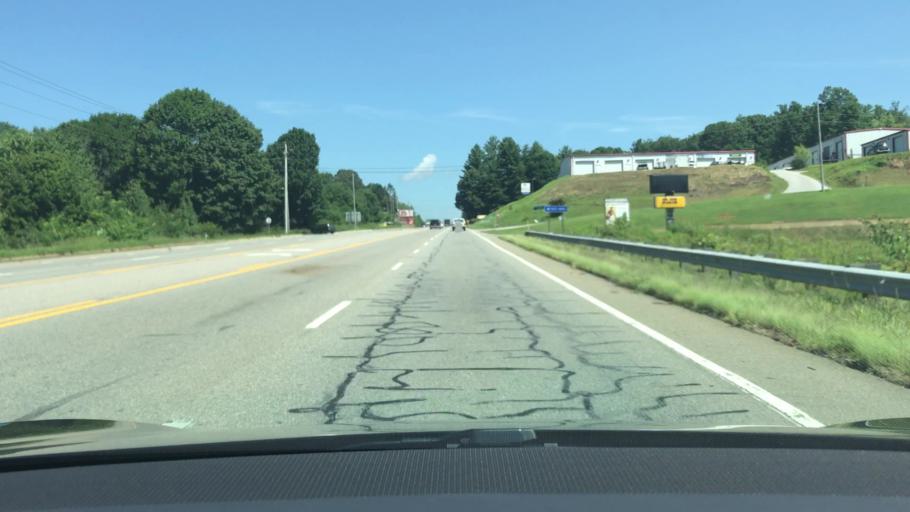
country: US
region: North Carolina
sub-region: Macon County
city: Franklin
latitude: 35.1126
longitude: -83.3893
